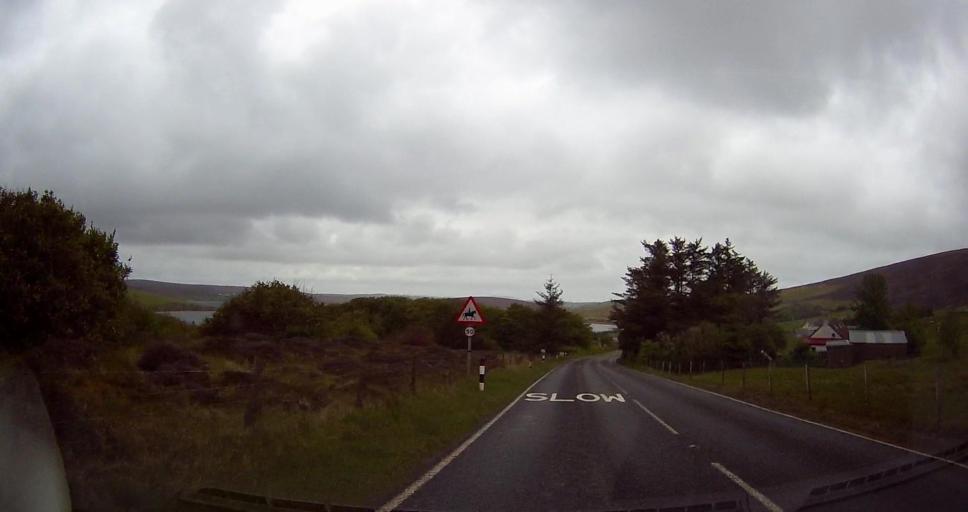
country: GB
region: Scotland
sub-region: Shetland Islands
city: Lerwick
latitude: 60.2415
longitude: -1.3419
